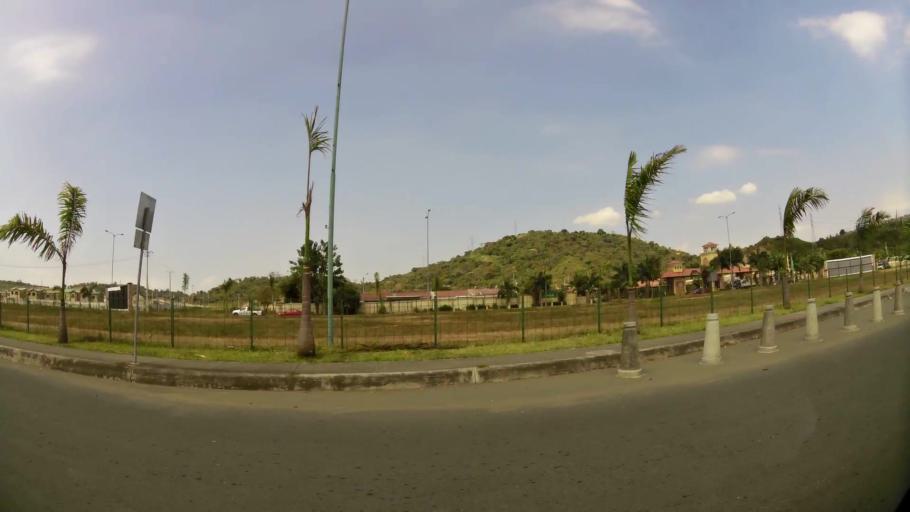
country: EC
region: Guayas
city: El Triunfo
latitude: -2.0318
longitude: -79.9142
